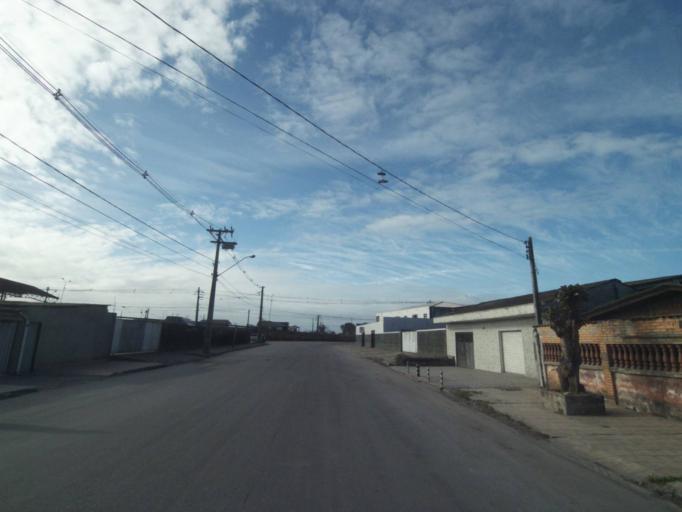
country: BR
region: Parana
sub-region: Paranagua
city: Paranagua
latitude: -25.5260
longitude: -48.5283
